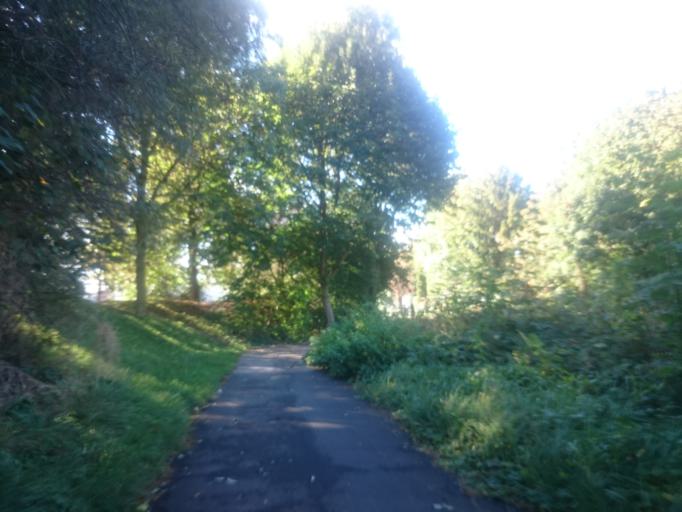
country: DE
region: Bavaria
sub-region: Swabia
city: Augsburg
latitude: 48.3659
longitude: 10.9247
